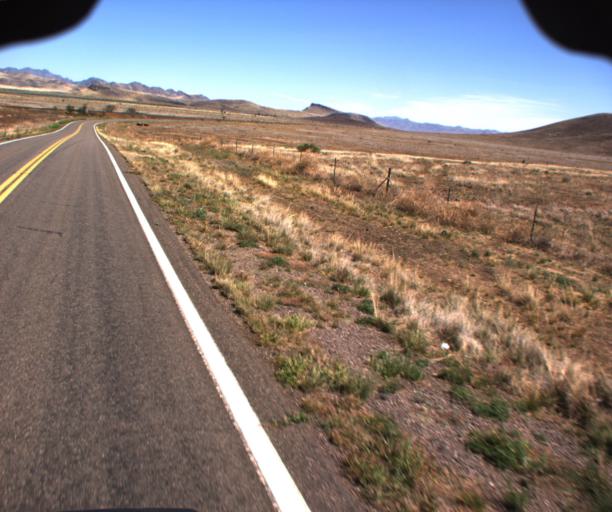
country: US
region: Arizona
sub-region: Cochise County
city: Douglas
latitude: 31.6169
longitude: -109.2152
